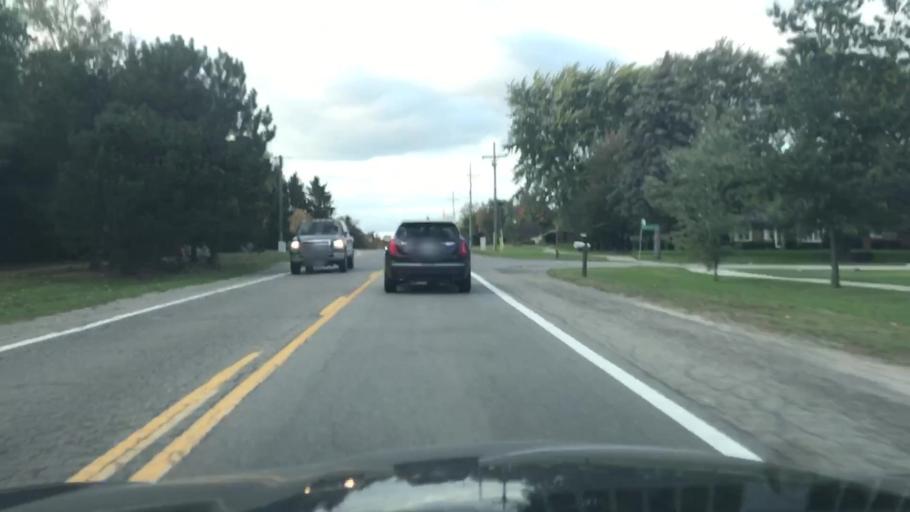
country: US
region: Michigan
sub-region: Oakland County
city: Rochester
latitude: 42.6861
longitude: -83.0943
